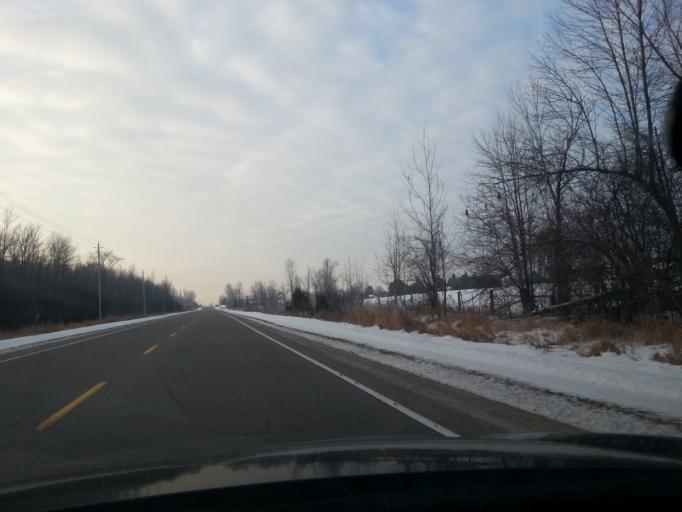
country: CA
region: Ontario
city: Perth
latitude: 44.9470
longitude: -76.2370
